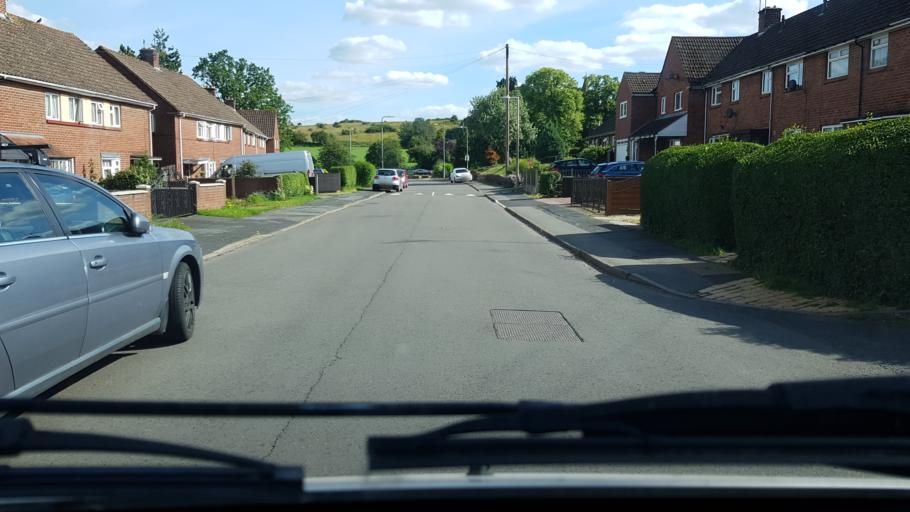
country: GB
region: England
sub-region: Worcestershire
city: Bewdley
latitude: 52.3802
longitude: -2.3049
